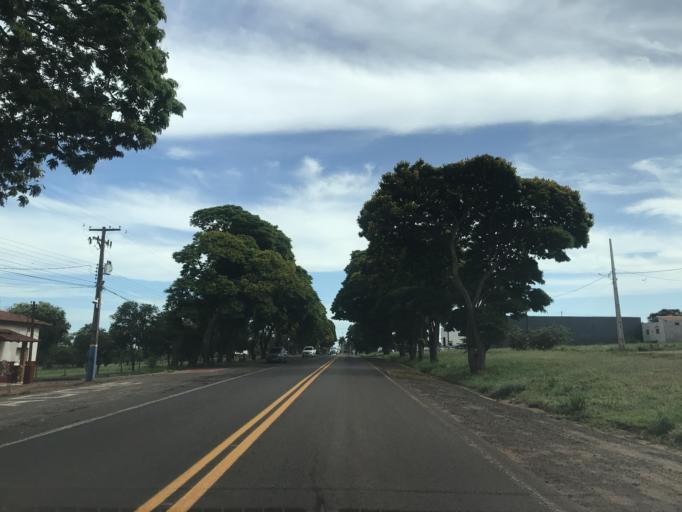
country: BR
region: Parana
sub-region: Terra Rica
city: Terra Rica
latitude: -22.7375
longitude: -52.6246
